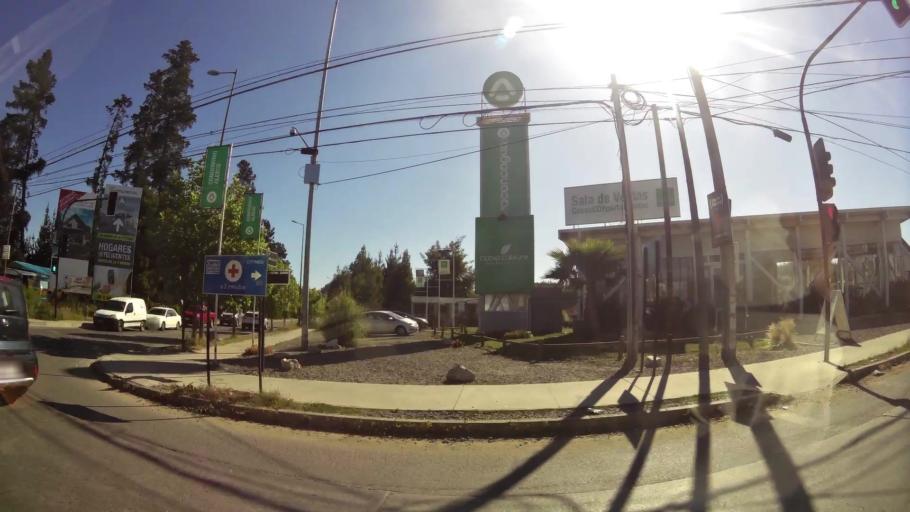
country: CL
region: Valparaiso
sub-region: Provincia de Valparaiso
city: Vina del Mar
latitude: -33.1317
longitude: -71.5652
